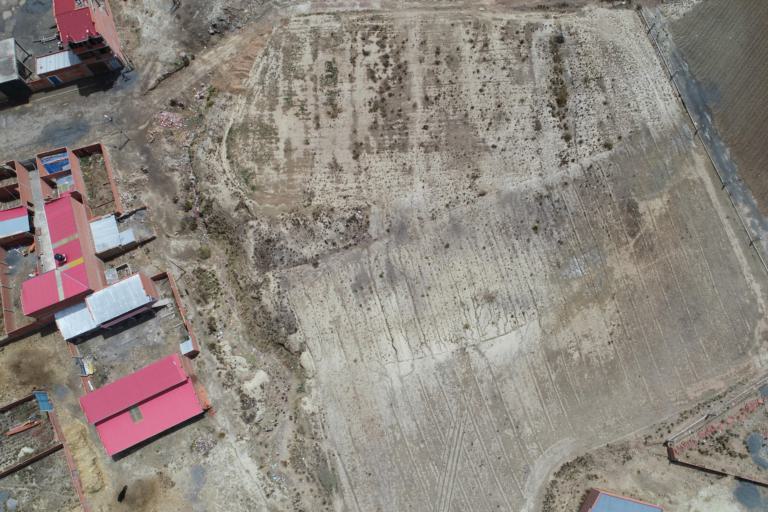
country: BO
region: La Paz
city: Achacachi
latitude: -16.0545
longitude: -68.6783
